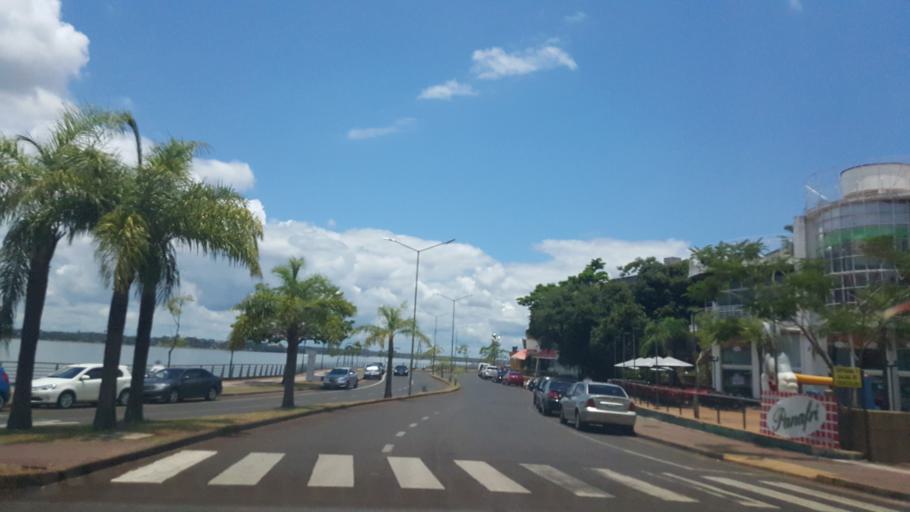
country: AR
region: Misiones
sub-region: Departamento de Capital
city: Posadas
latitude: -27.3584
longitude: -55.8909
